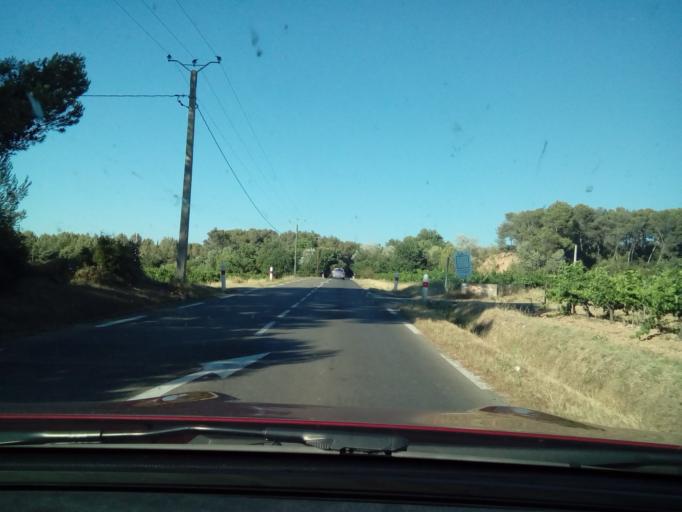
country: FR
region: Provence-Alpes-Cote d'Azur
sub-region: Departement des Bouches-du-Rhone
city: Trets
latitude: 43.4625
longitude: 5.7189
